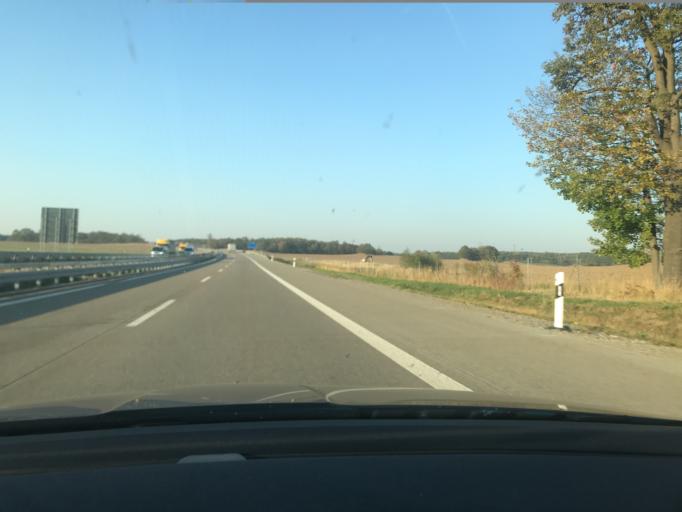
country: DE
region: Saxony
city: Radeburg
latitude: 51.1650
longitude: 13.7504
